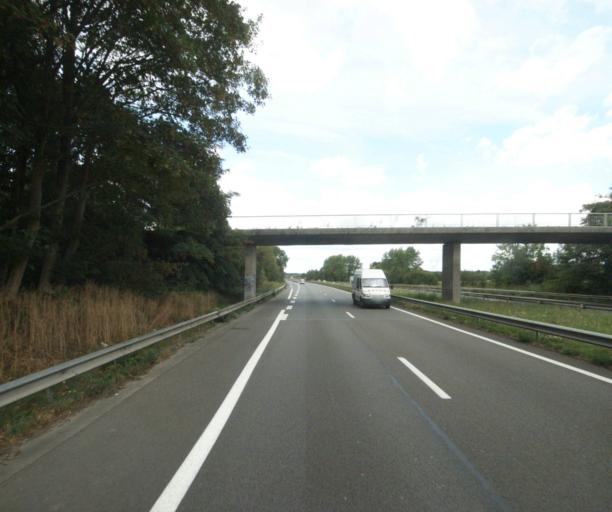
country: FR
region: Nord-Pas-de-Calais
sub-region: Departement du Nord
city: Genech
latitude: 50.5116
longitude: 3.2105
